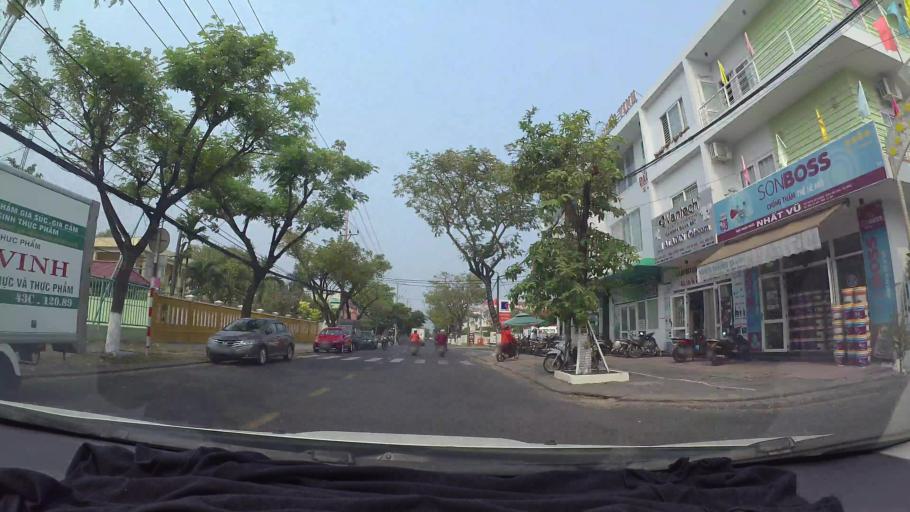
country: VN
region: Da Nang
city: Da Nang
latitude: 16.0466
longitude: 108.2111
